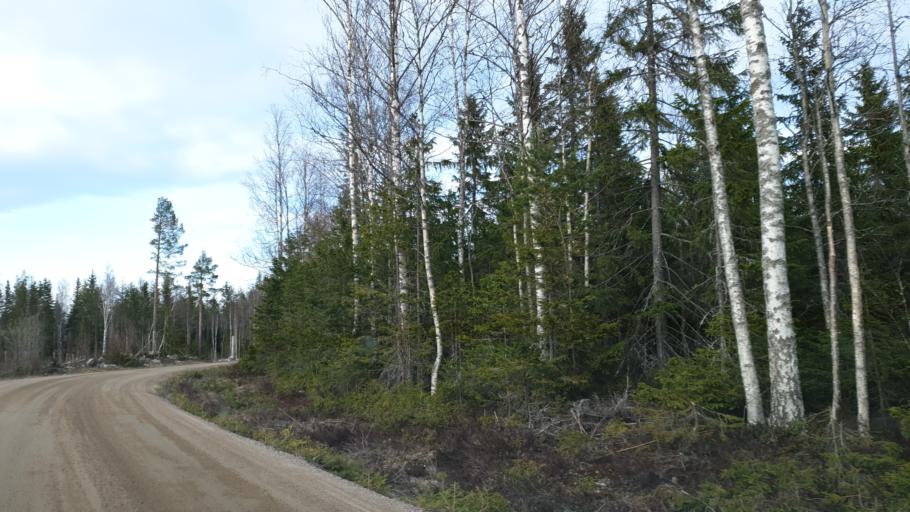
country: SE
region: Vaesternorrland
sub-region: Sundsvalls Kommun
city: Njurundabommen
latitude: 62.1504
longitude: 17.4264
